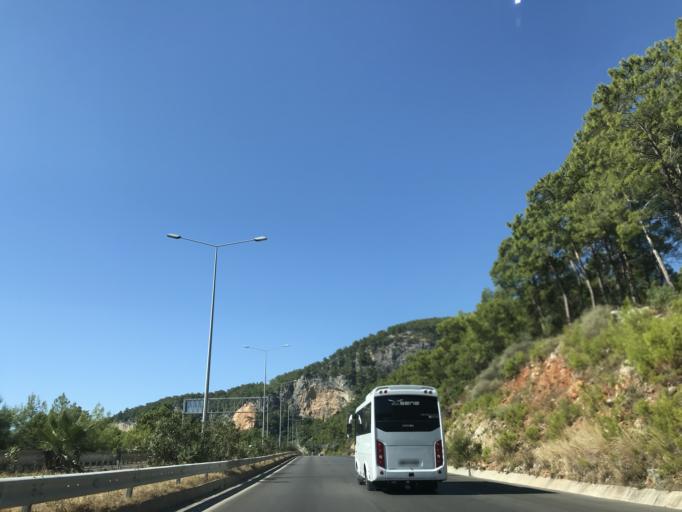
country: TR
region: Antalya
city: Cakirlar
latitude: 36.7572
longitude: 30.5692
